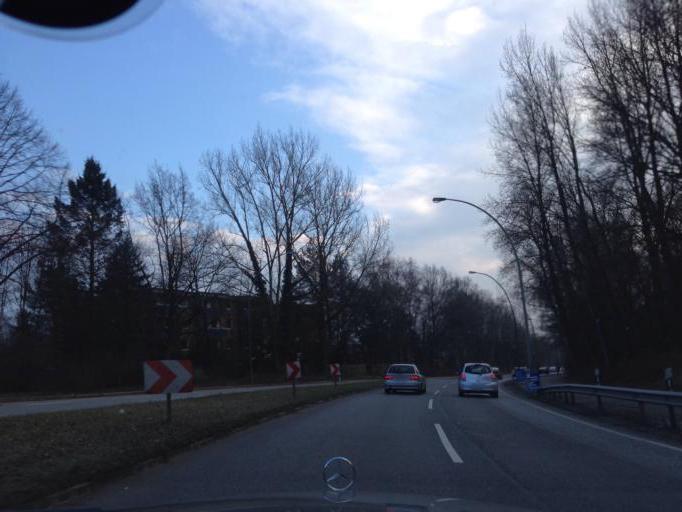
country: DE
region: Schleswig-Holstein
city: Glinde
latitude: 53.5060
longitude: 10.1839
